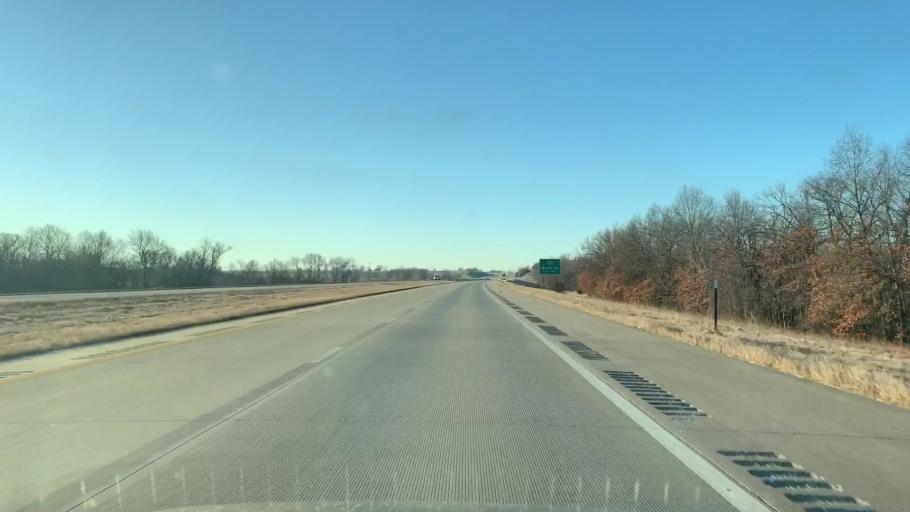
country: US
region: Kansas
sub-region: Linn County
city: Pleasanton
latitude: 38.0137
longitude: -94.7039
